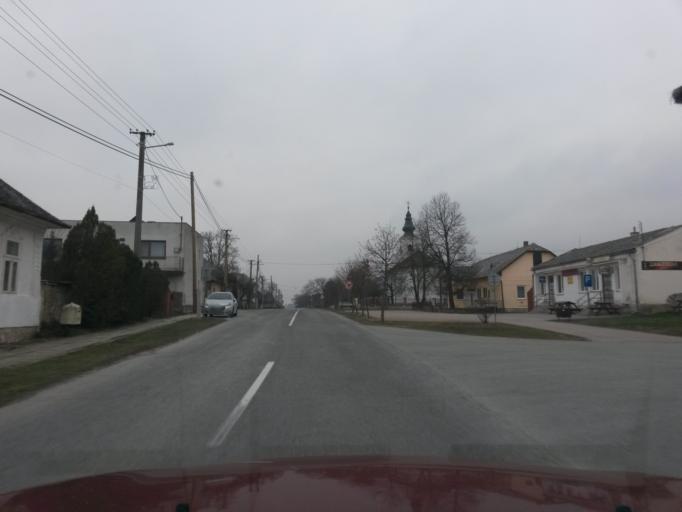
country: SK
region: Kosicky
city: Medzev
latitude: 48.6022
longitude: 20.8387
